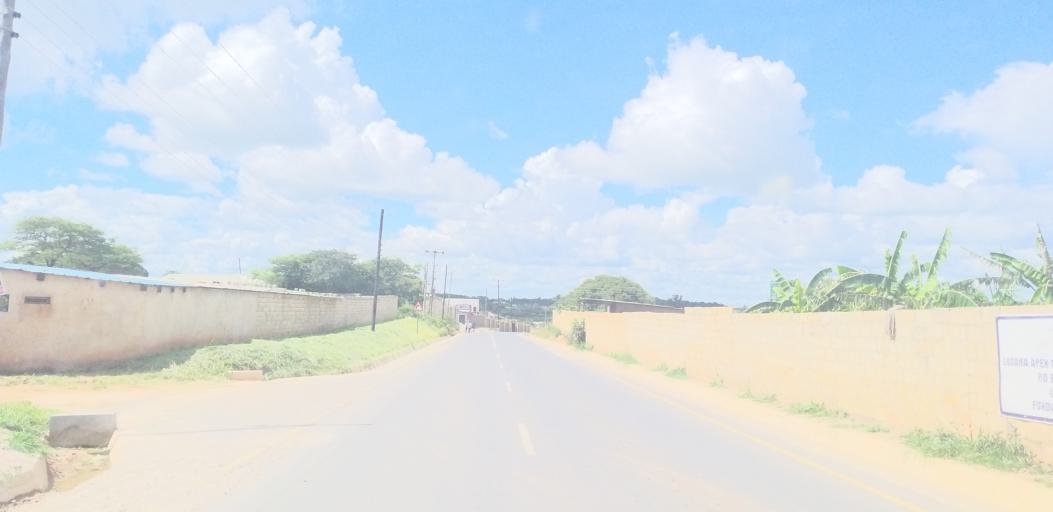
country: ZM
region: Lusaka
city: Lusaka
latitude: -15.3421
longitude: 28.3283
